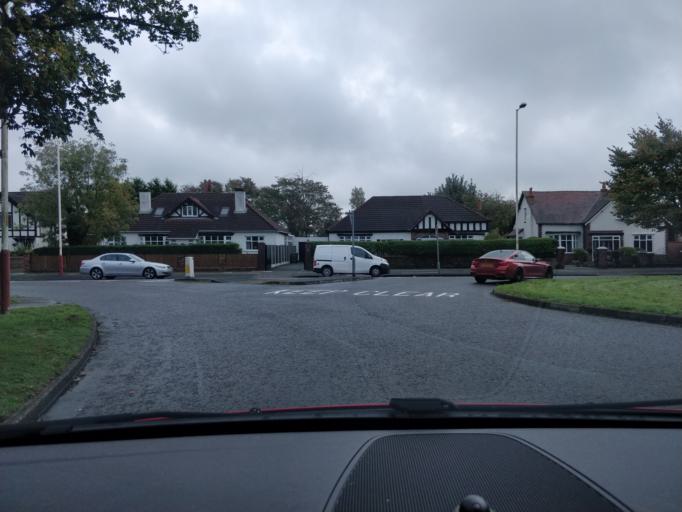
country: GB
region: England
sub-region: Sefton
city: Southport
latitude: 53.6136
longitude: -3.0199
